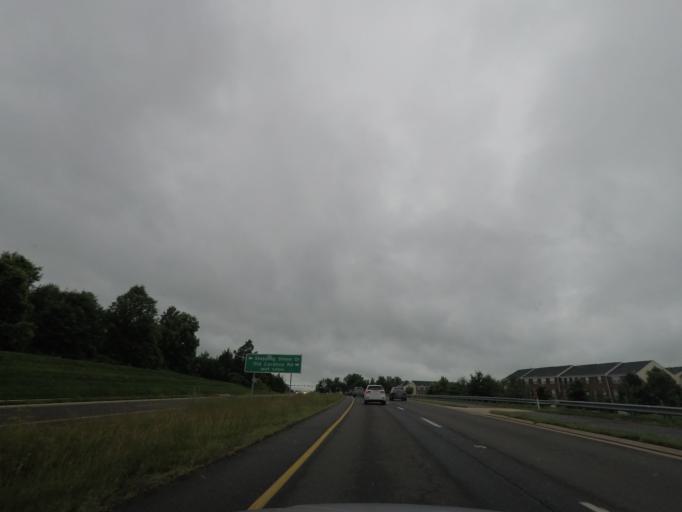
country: US
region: Virginia
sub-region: Prince William County
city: Haymarket
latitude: 38.8238
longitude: -77.6340
